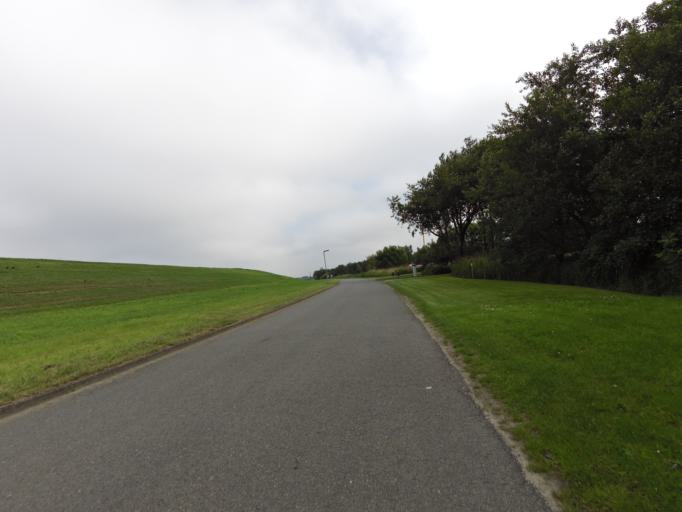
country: DE
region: Lower Saxony
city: Padingbuttel
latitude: 53.7434
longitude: 8.5259
